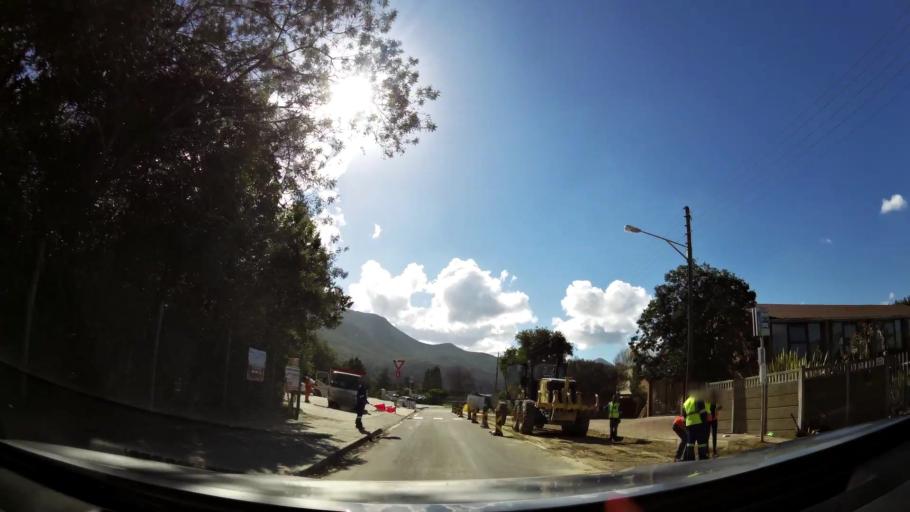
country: ZA
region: Western Cape
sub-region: Eden District Municipality
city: George
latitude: -33.9472
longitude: 22.4647
